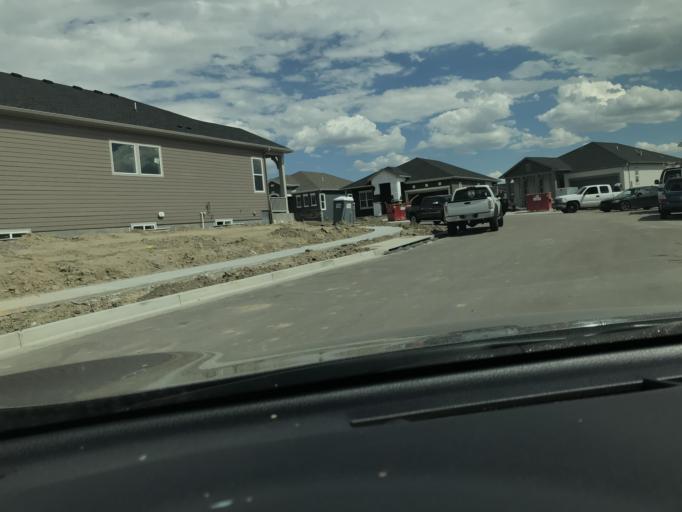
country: US
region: Colorado
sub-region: El Paso County
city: Black Forest
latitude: 38.9644
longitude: -104.7044
